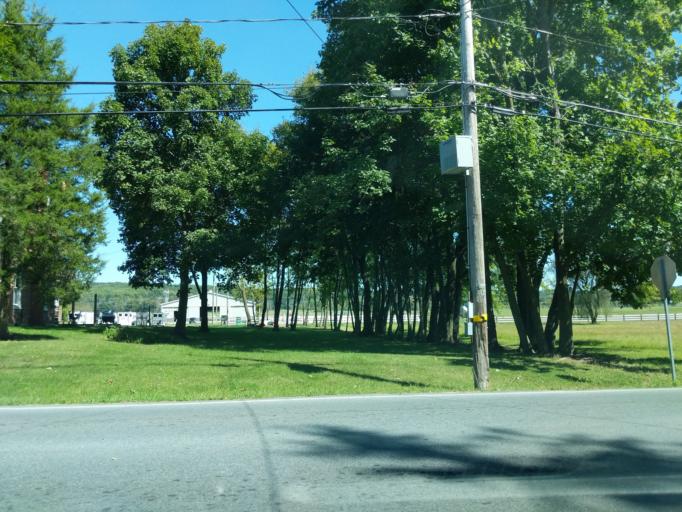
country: US
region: Pennsylvania
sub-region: Montgomery County
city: East Greenville
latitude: 40.4316
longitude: -75.4852
